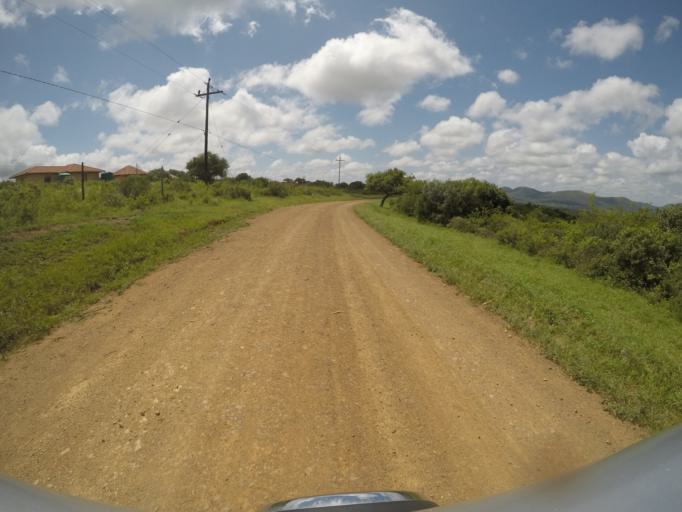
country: ZA
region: KwaZulu-Natal
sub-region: uThungulu District Municipality
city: Empangeni
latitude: -28.5869
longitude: 31.8219
